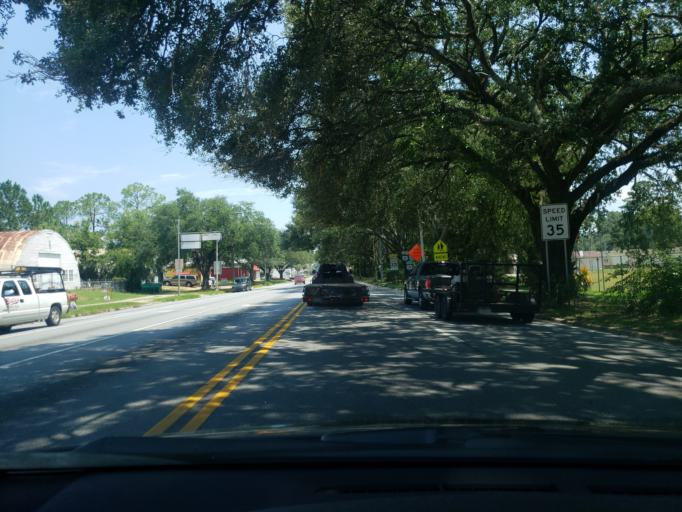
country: US
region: Georgia
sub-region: Dougherty County
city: Albany
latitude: 31.5753
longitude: -84.1759
